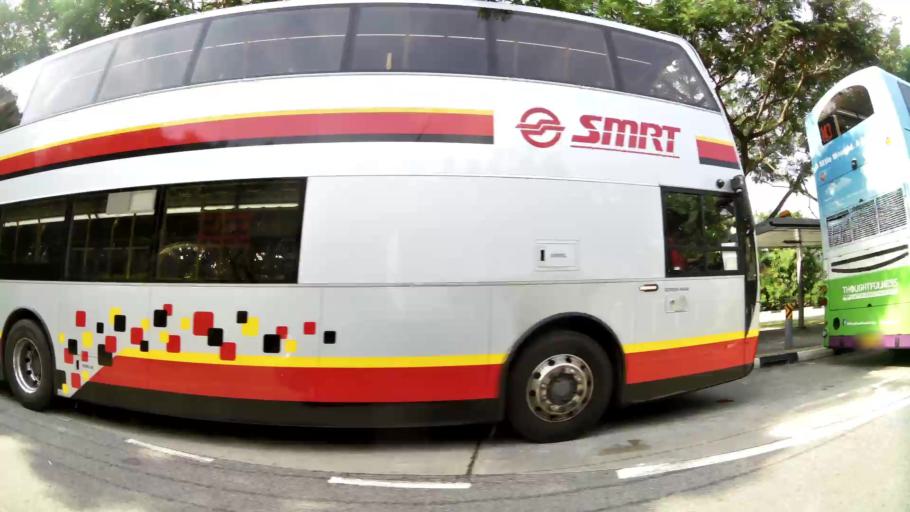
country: SG
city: Singapore
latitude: 1.2828
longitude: 103.7819
